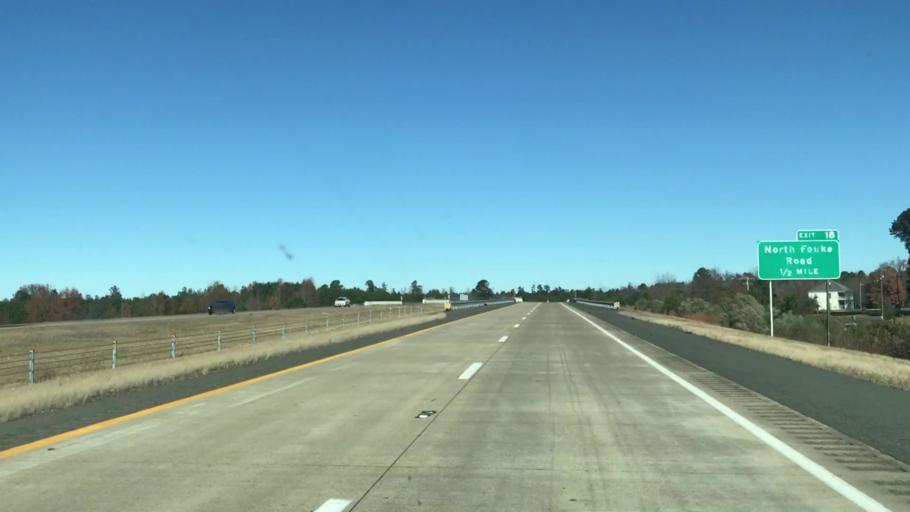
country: US
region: Texas
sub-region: Bowie County
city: Texarkana
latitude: 33.2569
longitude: -93.8948
